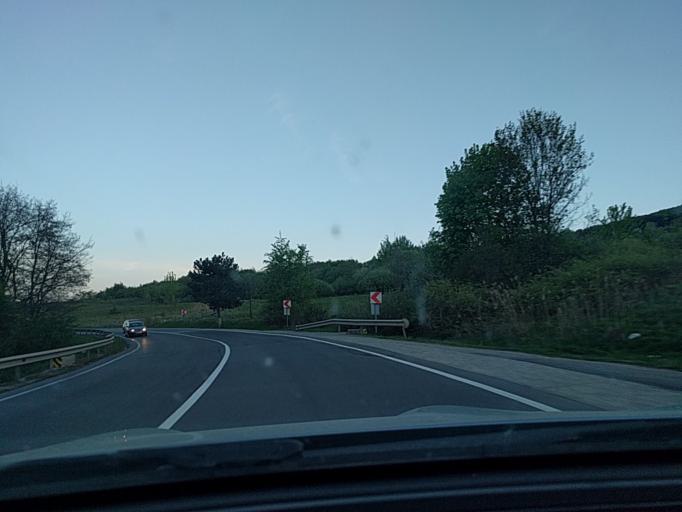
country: RO
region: Mures
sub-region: Comuna Nades
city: Nades
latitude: 46.2869
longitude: 24.7219
